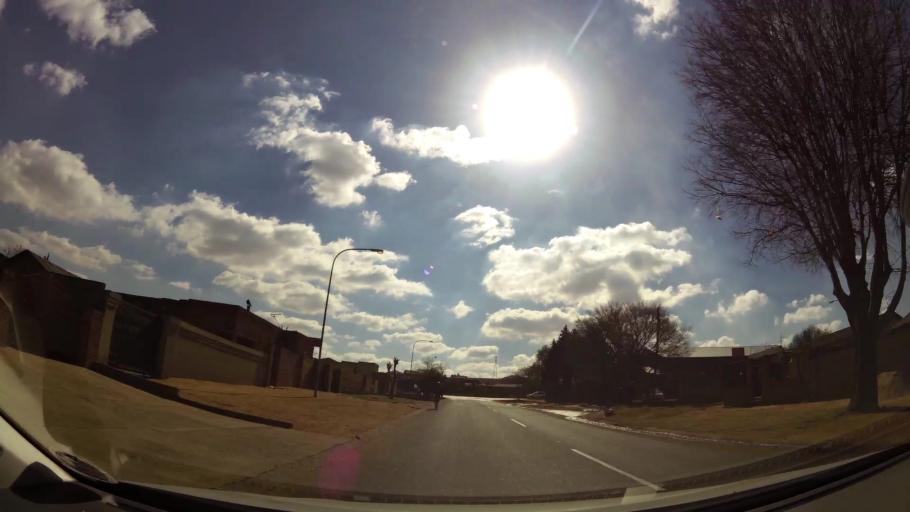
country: ZA
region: Gauteng
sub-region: City of Johannesburg Metropolitan Municipality
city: Roodepoort
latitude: -26.2071
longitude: 27.8808
